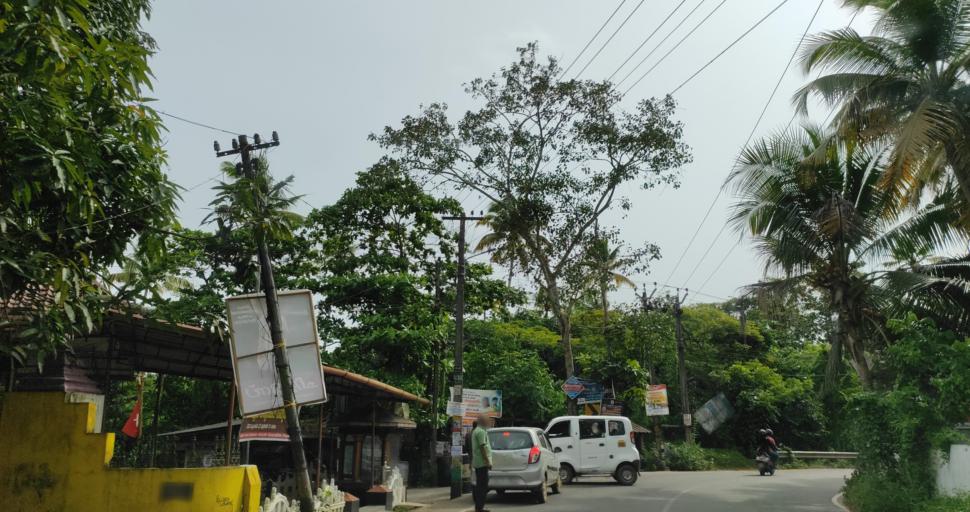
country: IN
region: Kerala
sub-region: Alappuzha
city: Shertallai
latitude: 9.6758
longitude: 76.3835
